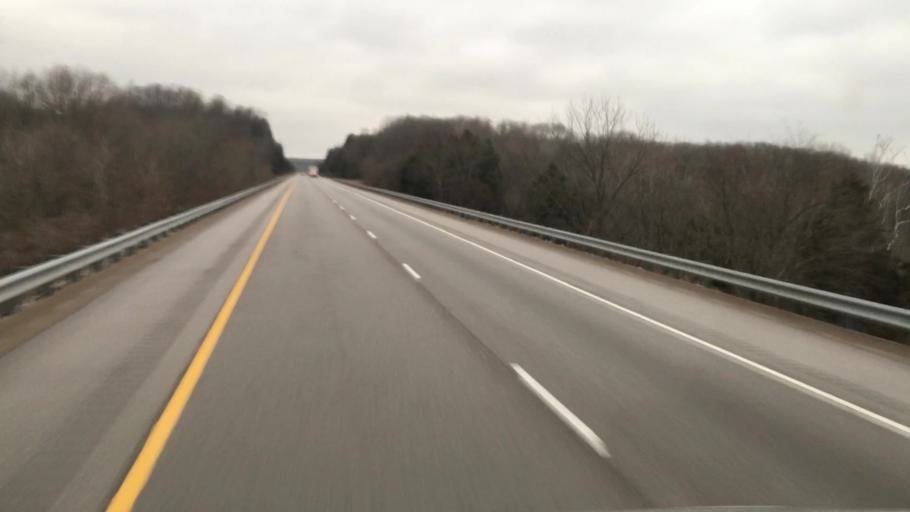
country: US
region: Illinois
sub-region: Johnson County
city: Vienna
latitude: 37.4760
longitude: -88.8918
